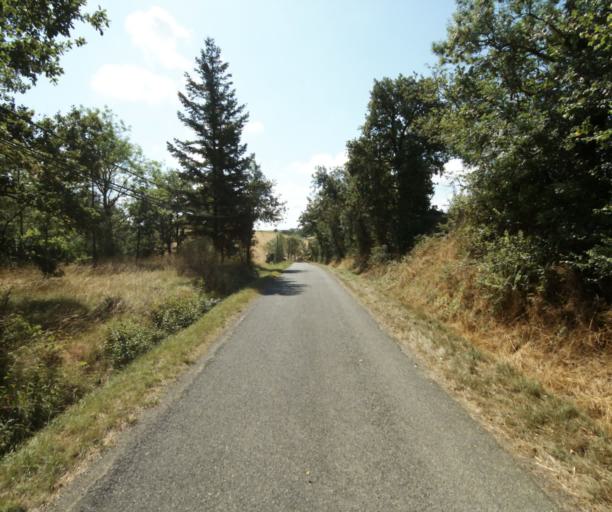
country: FR
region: Midi-Pyrenees
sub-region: Departement de la Haute-Garonne
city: Auriac-sur-Vendinelle
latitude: 43.4585
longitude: 1.7863
